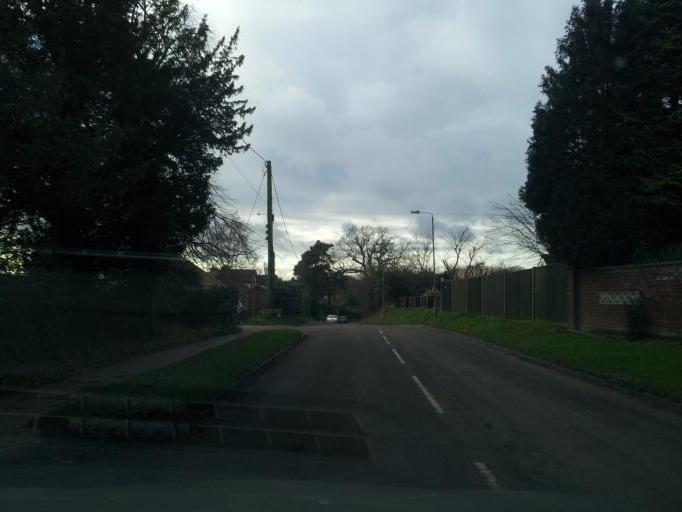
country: GB
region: England
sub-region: Norfolk
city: Brundall
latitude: 52.6256
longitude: 1.4207
